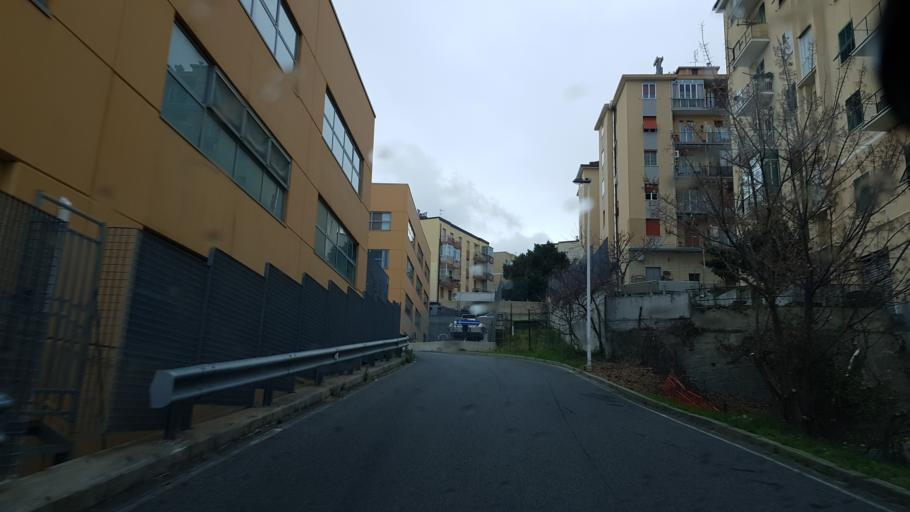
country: IT
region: Liguria
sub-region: Provincia di Savona
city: Savona
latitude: 44.3002
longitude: 8.4595
